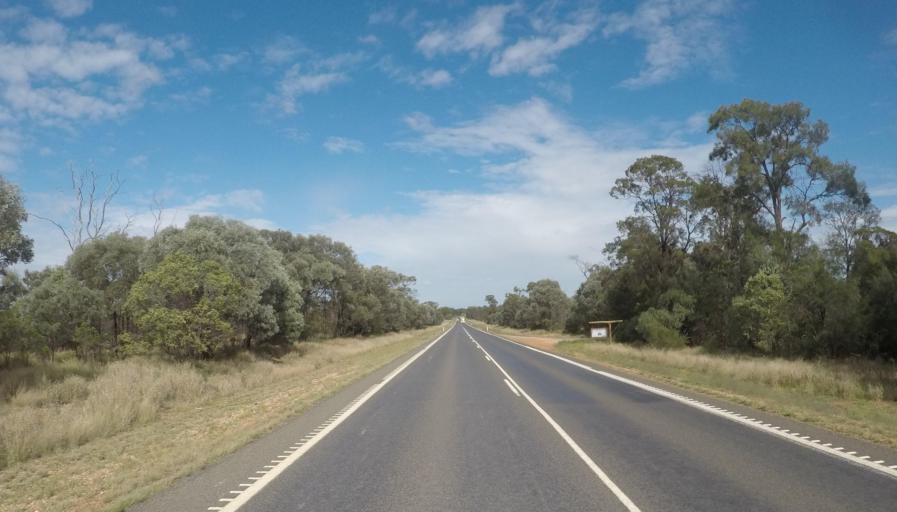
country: AU
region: Queensland
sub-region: Western Downs
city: Westcourt
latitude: -26.6418
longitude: 149.6376
